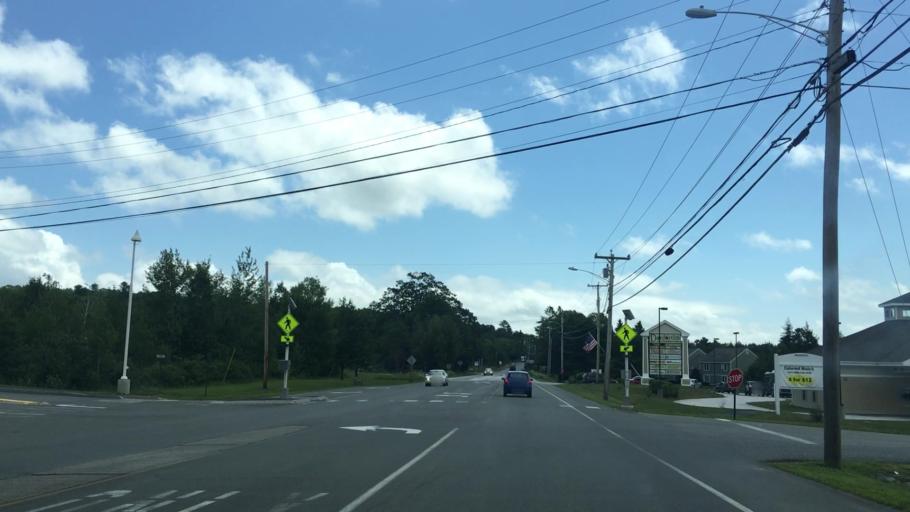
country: US
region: Maine
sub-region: Penobscot County
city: Hermon
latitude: 44.8062
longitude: -68.9032
